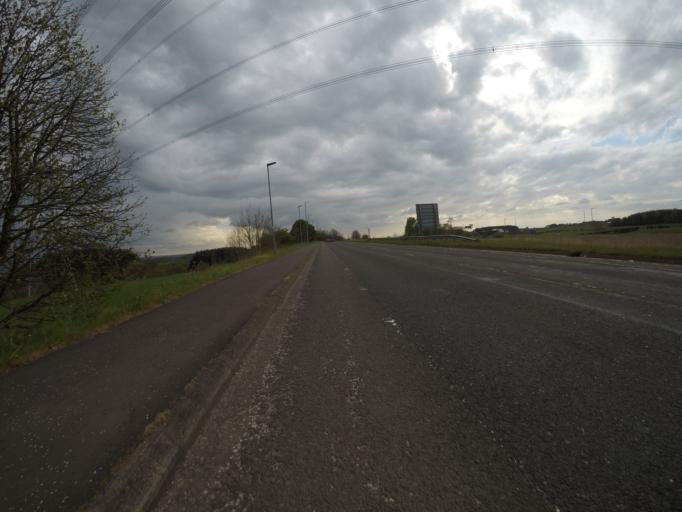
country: GB
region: Scotland
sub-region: East Ayrshire
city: Kilmarnock
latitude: 55.6427
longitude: -4.4628
